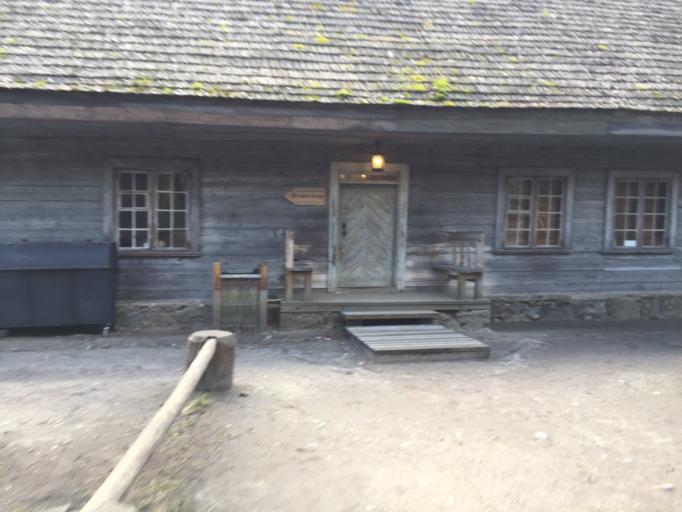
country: LV
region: Riga
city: Bergi
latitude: 56.9945
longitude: 24.2711
